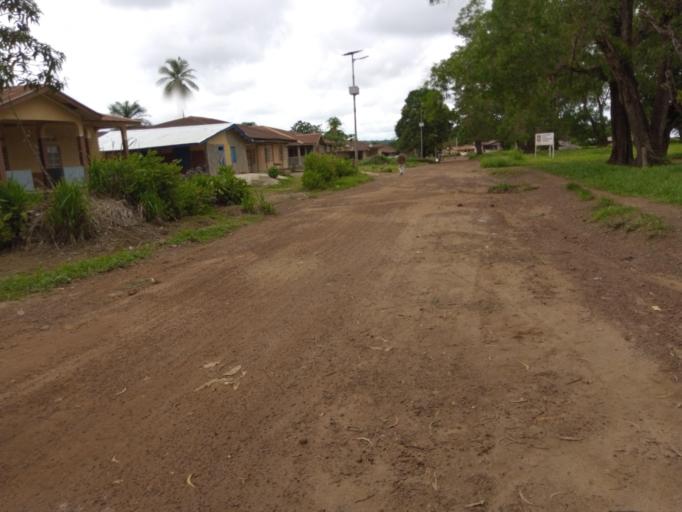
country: SL
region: Southern Province
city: Moyamba
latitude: 8.1657
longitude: -12.4246
